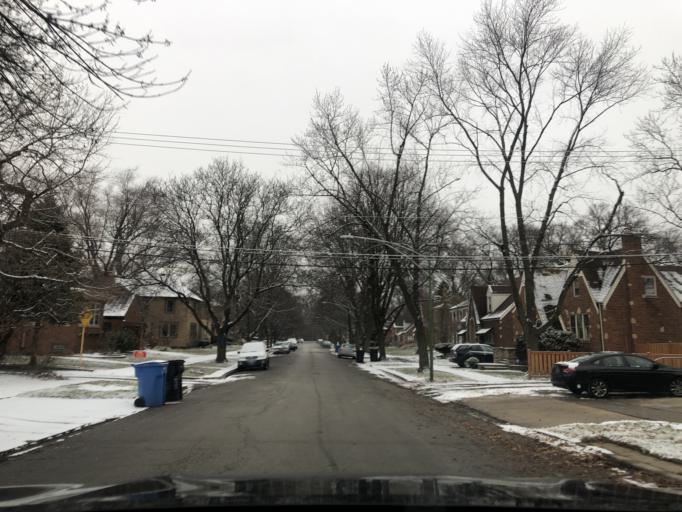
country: US
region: Illinois
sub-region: Cook County
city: Evergreen Park
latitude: 41.7284
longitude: -87.6810
